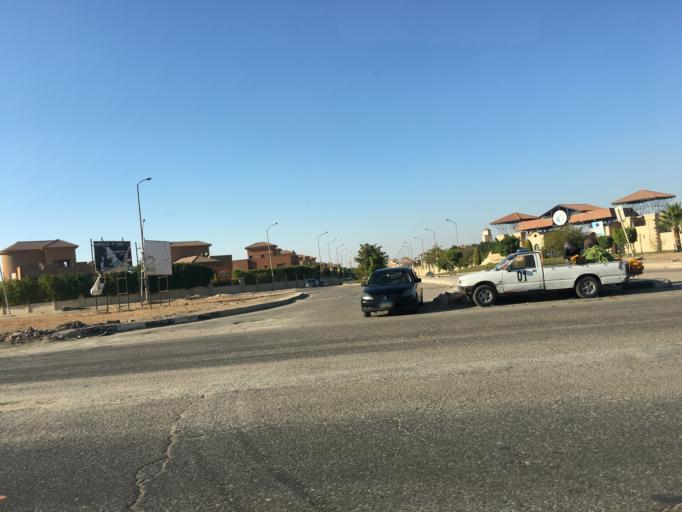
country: EG
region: Al Jizah
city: Madinat Sittah Uktubar
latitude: 29.9950
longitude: 30.9516
